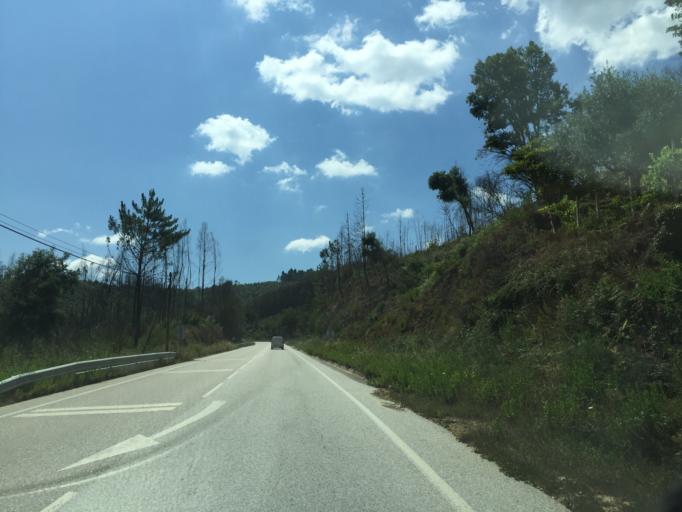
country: PT
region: Leiria
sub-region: Pedrogao Grande
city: Pedrogao Grande
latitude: 40.0056
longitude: -8.1135
